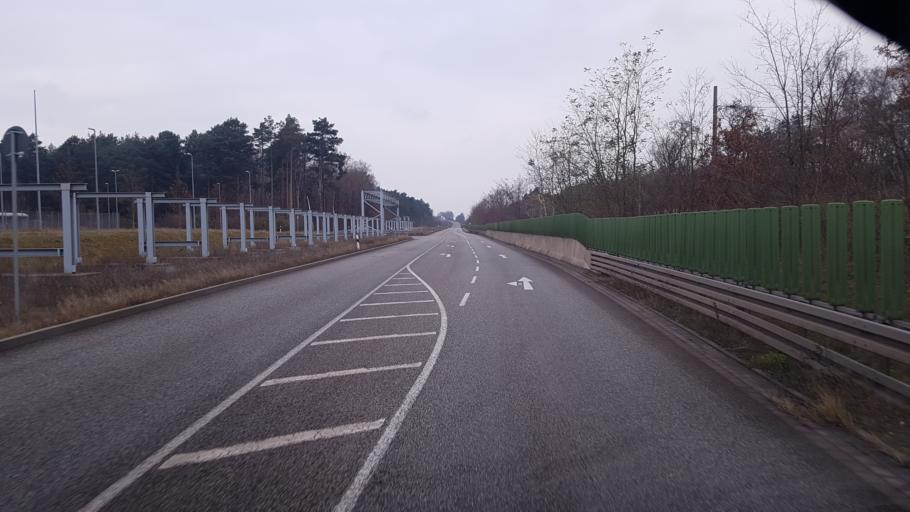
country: DE
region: Brandenburg
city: Ziltendorf
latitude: 52.1819
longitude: 14.6337
